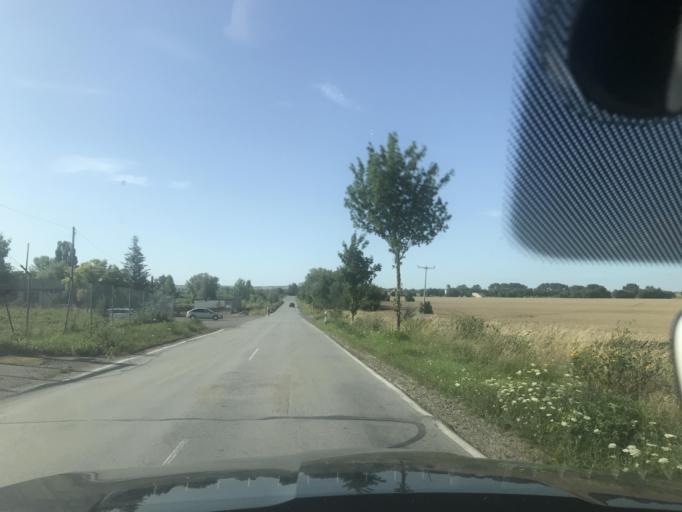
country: DE
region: Saxony-Anhalt
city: Wegeleben
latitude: 51.9010
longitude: 11.1552
